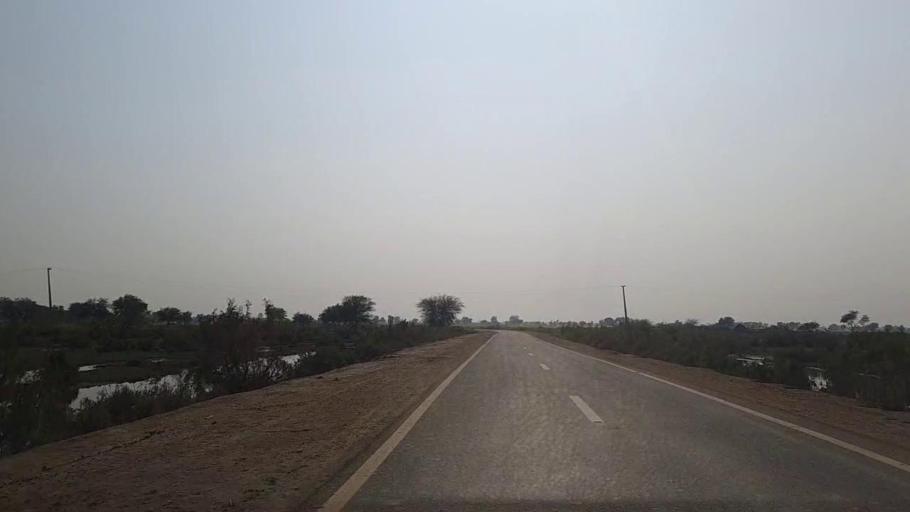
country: PK
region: Sindh
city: Jam Sahib
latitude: 26.3665
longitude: 68.5353
